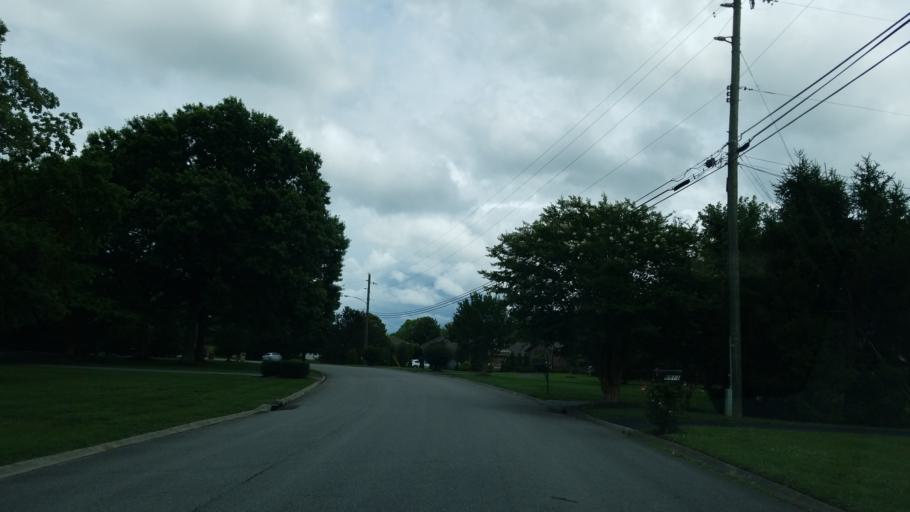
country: US
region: Tennessee
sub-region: Williamson County
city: Brentwood
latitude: 36.0270
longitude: -86.8214
